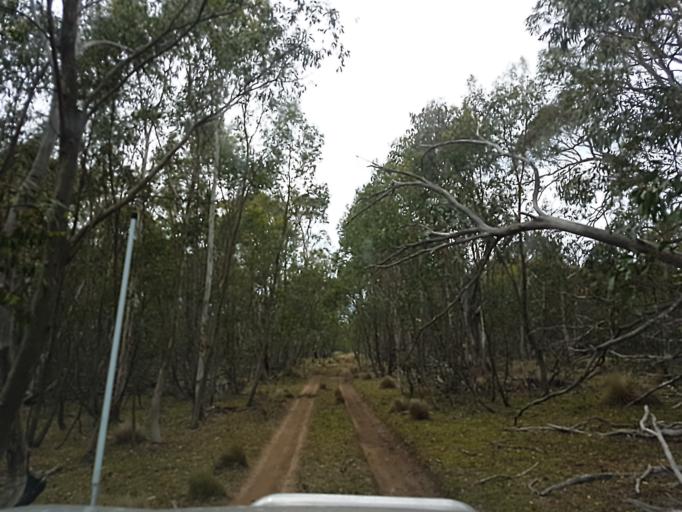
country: AU
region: New South Wales
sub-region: Snowy River
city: Jindabyne
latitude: -36.8540
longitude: 148.2606
